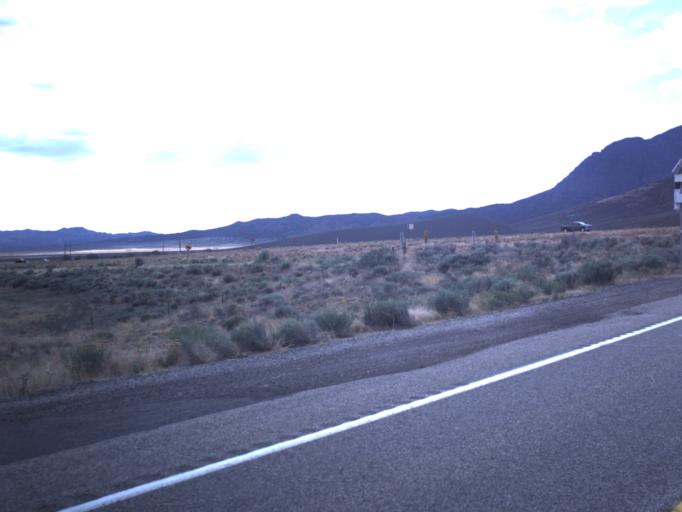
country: US
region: Utah
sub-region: Beaver County
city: Beaver
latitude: 38.0709
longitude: -112.6859
